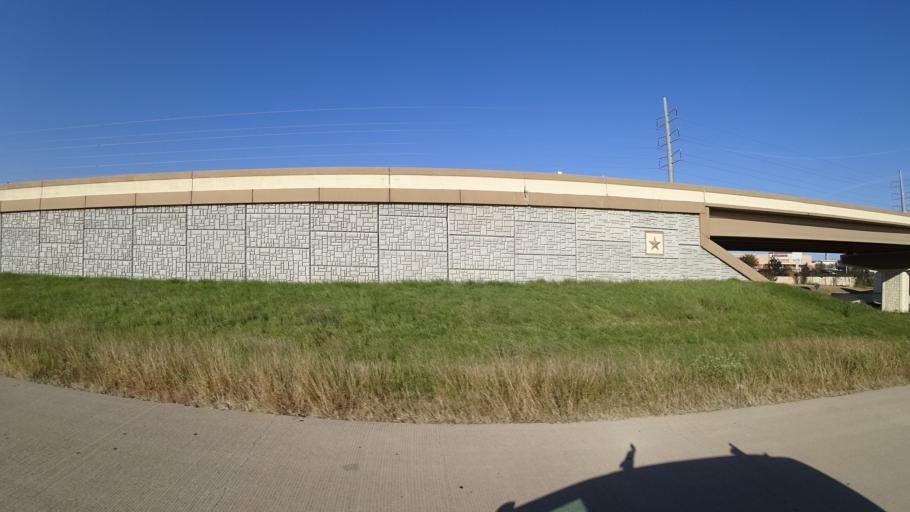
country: US
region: Texas
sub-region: Travis County
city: Pflugerville
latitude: 30.4702
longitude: -97.5939
